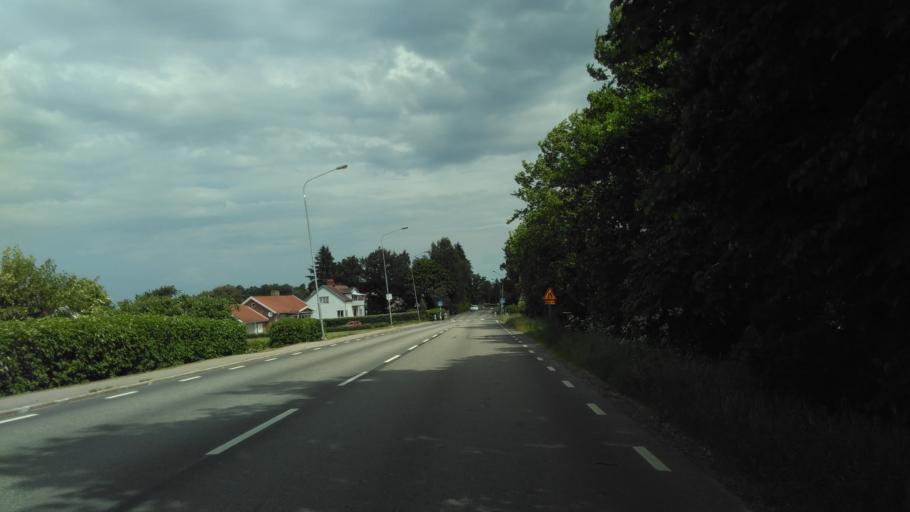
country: SE
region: Vaestra Goetaland
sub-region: Vara Kommun
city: Kvanum
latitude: 58.3827
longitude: 13.1477
